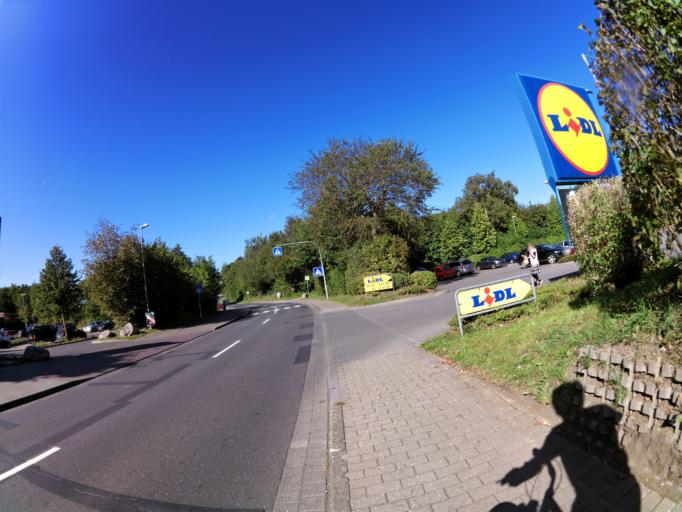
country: DE
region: Schleswig-Holstein
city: Barkelsby
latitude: 54.4873
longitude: 9.8248
